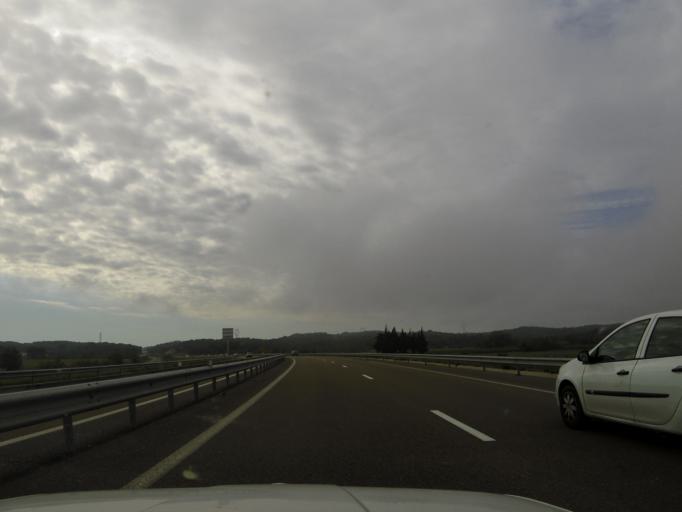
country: FR
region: Languedoc-Roussillon
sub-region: Departement du Gard
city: La Calmette
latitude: 43.9235
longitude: 4.2550
